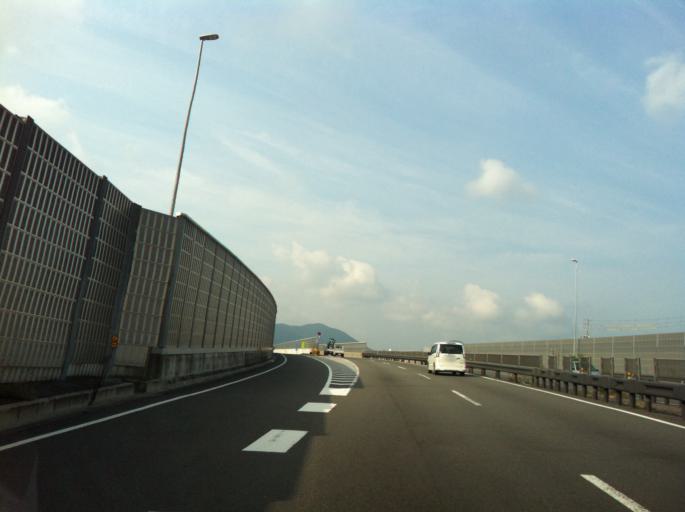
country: JP
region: Shizuoka
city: Shizuoka-shi
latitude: 34.9997
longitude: 138.3693
